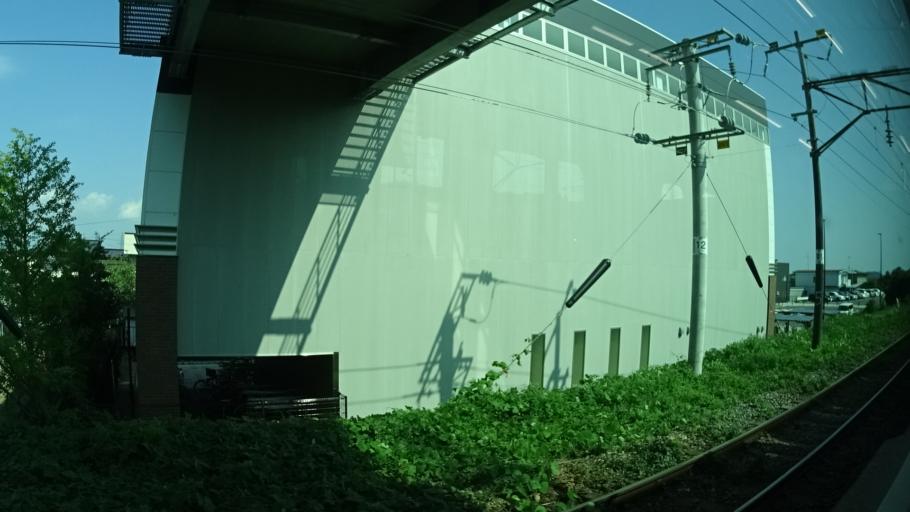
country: JP
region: Miyagi
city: Wakuya
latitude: 38.4747
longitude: 141.0982
